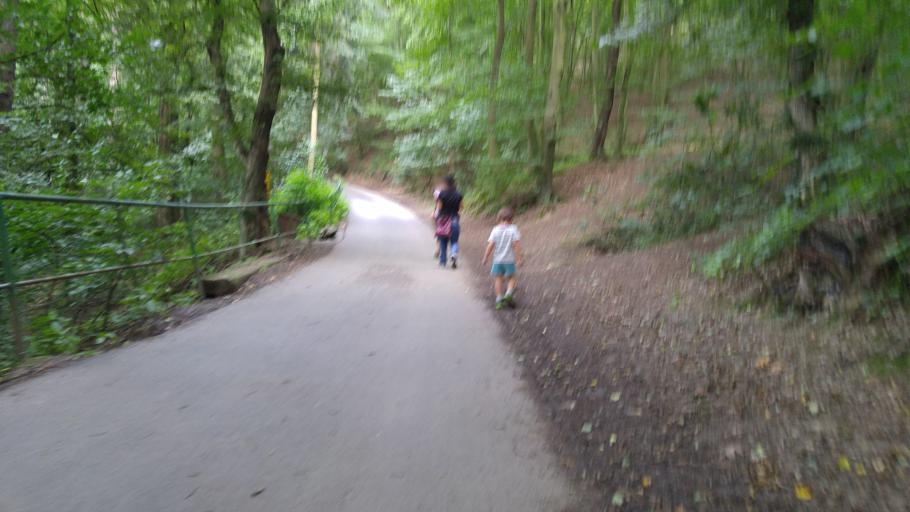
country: CZ
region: Central Bohemia
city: Horomerice
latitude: 50.1027
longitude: 14.3318
